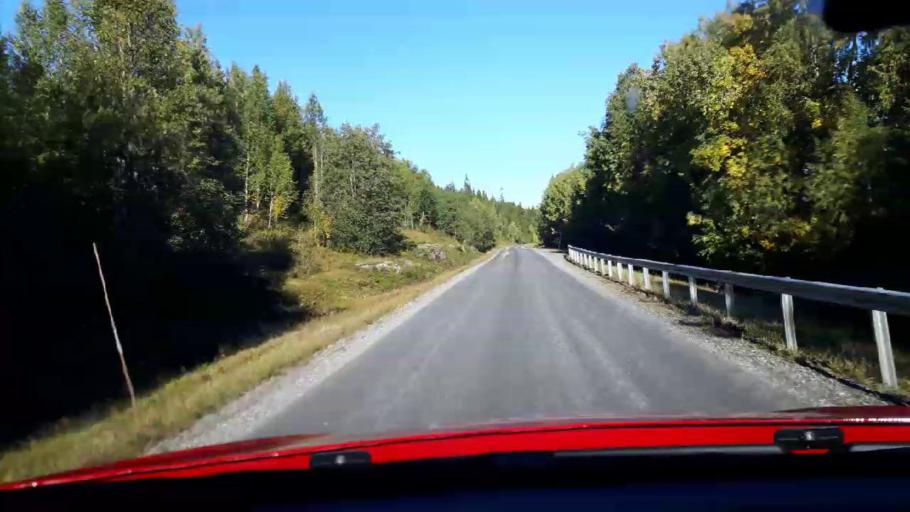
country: NO
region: Nord-Trondelag
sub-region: Lierne
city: Sandvika
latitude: 64.5732
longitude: 13.9009
